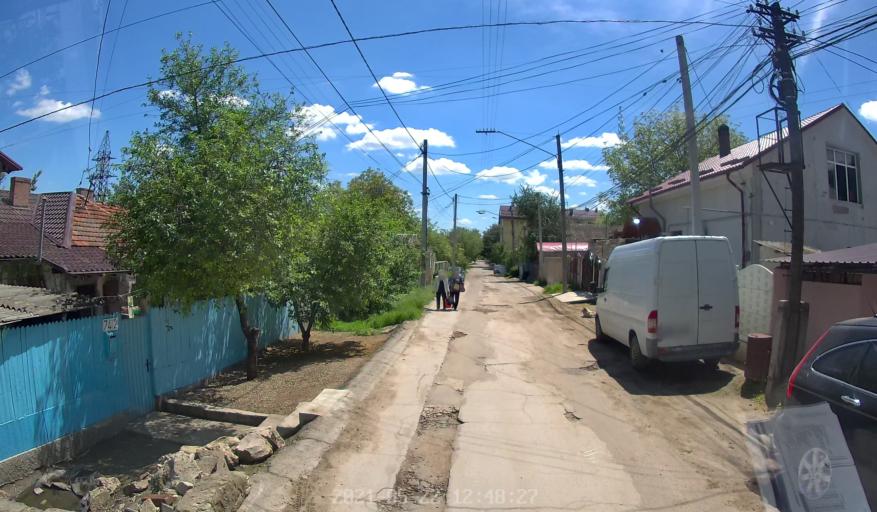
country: MD
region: Chisinau
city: Chisinau
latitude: 47.0501
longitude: 28.8351
